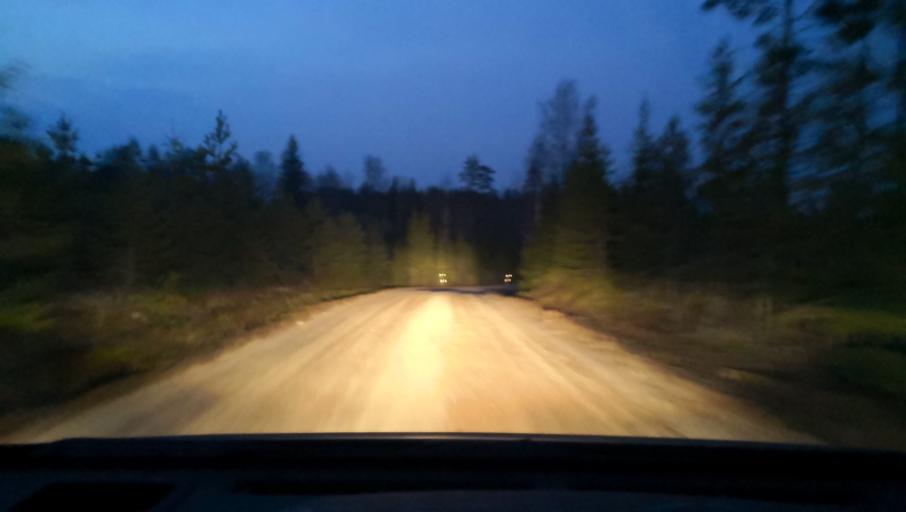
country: SE
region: OErebro
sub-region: Lindesbergs Kommun
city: Frovi
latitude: 59.6019
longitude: 15.4708
